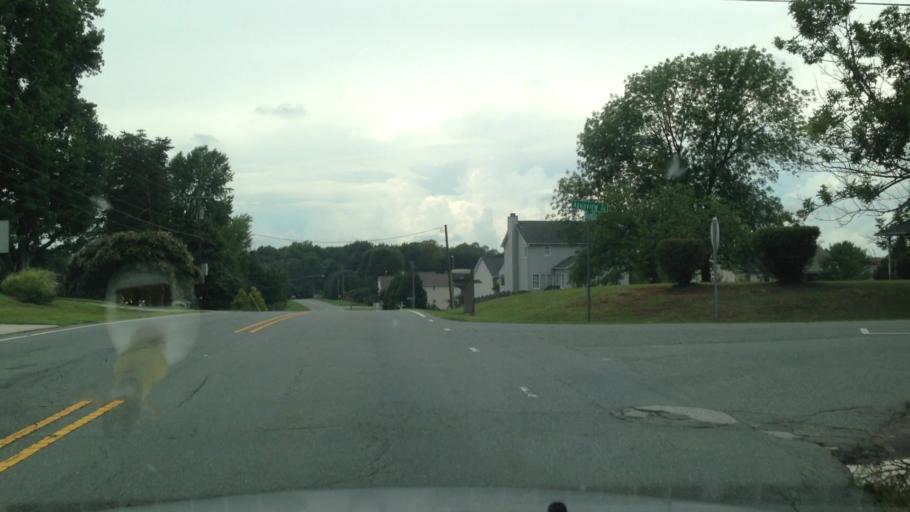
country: US
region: North Carolina
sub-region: Forsyth County
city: Kernersville
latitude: 36.1398
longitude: -80.0762
